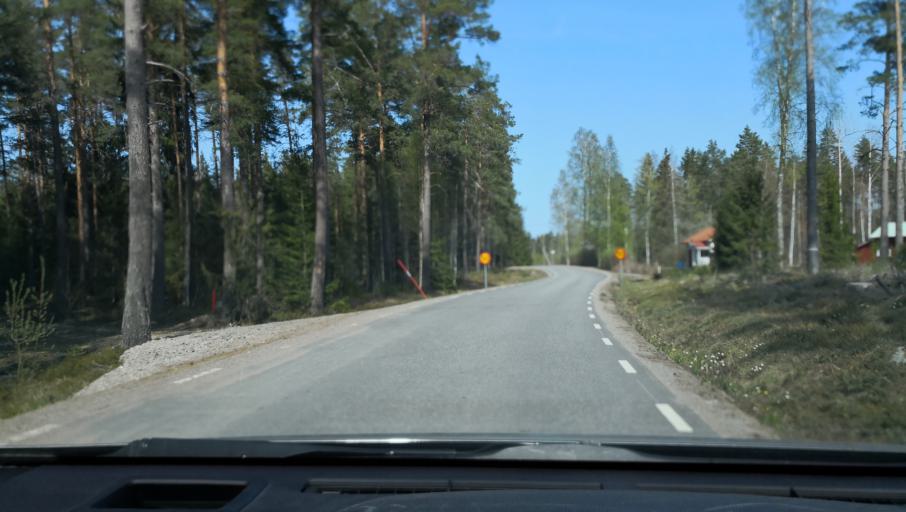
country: SE
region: Vaestmanland
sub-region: Sala Kommun
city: Sala
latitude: 60.0035
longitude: 16.6697
